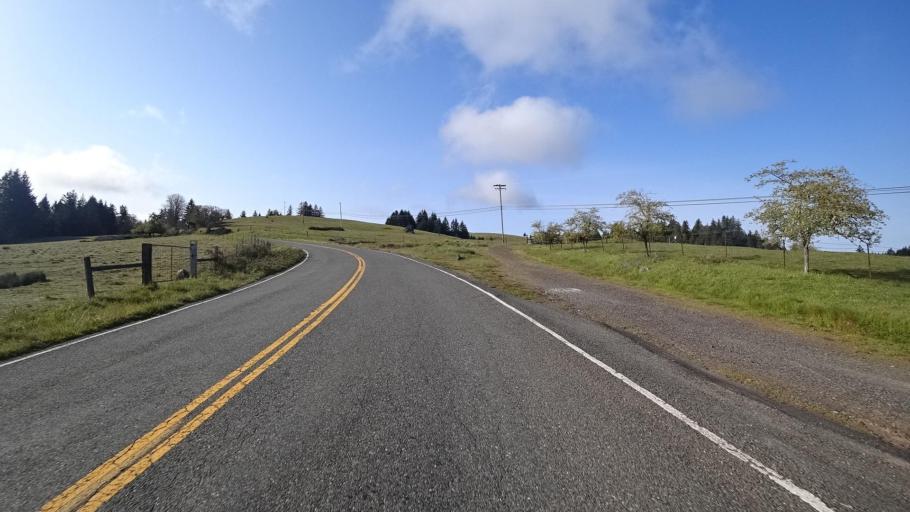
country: US
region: California
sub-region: Humboldt County
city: Blue Lake
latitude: 40.7304
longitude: -123.9480
